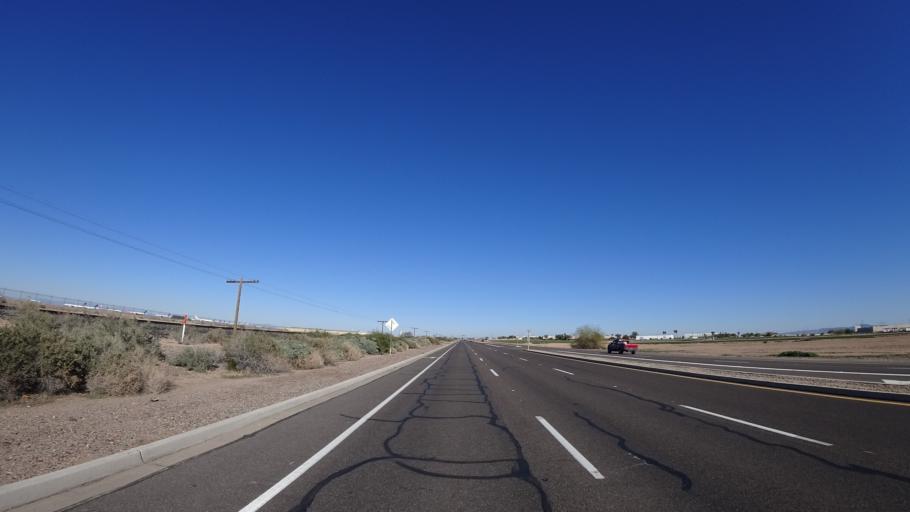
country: US
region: Arizona
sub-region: Maricopa County
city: Goodyear
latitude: 33.4112
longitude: -112.3820
